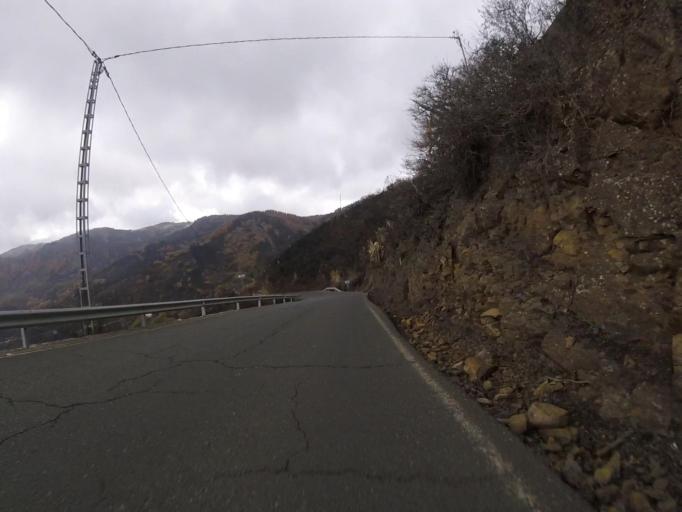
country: ES
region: Canary Islands
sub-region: Provincia de Las Palmas
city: Tejeda
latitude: 27.9888
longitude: -15.5757
